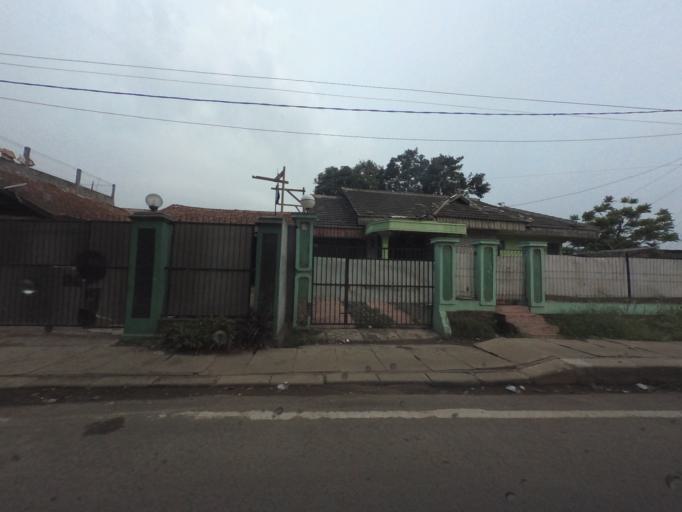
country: ID
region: West Java
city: Cicurug
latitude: -6.7568
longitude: 106.7991
